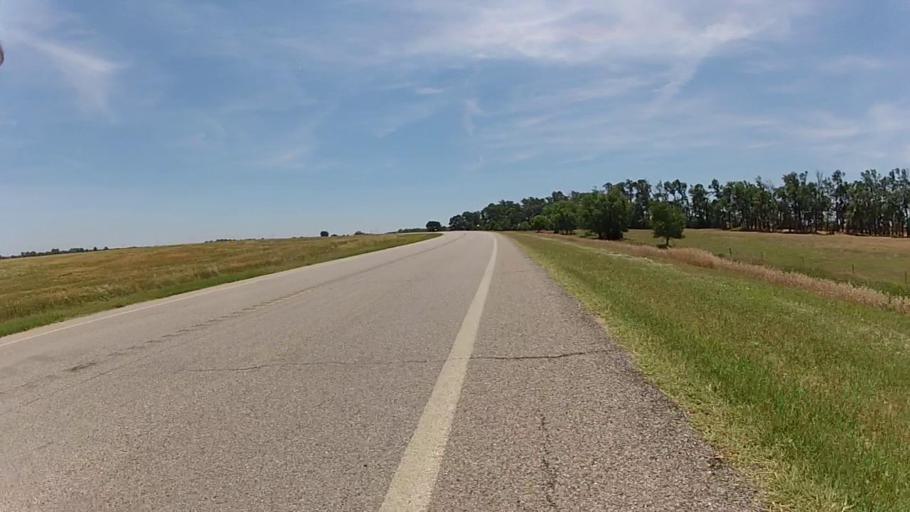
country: US
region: Kansas
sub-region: Barber County
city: Medicine Lodge
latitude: 37.2555
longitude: -98.5218
